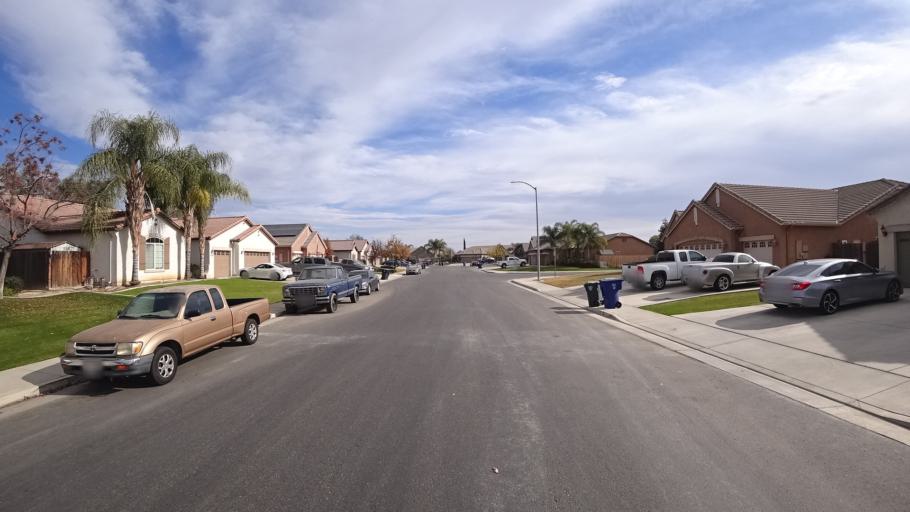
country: US
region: California
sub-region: Kern County
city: Rosedale
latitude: 35.4219
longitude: -119.1426
